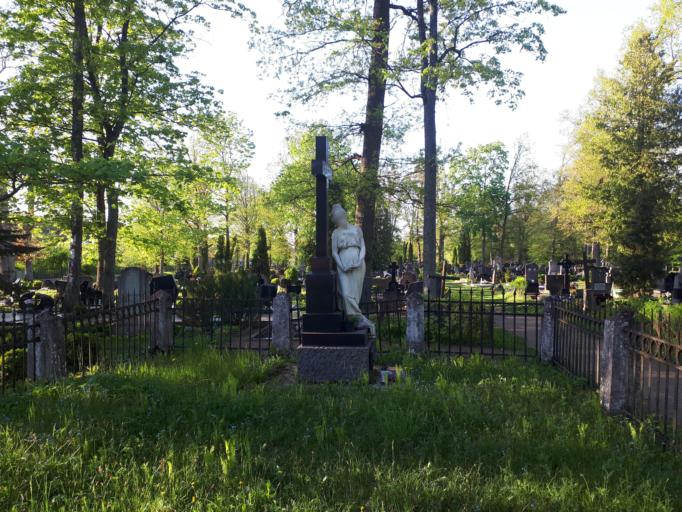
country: LT
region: Alytaus apskritis
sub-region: Alytus
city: Alytus
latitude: 54.4669
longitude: 24.0547
